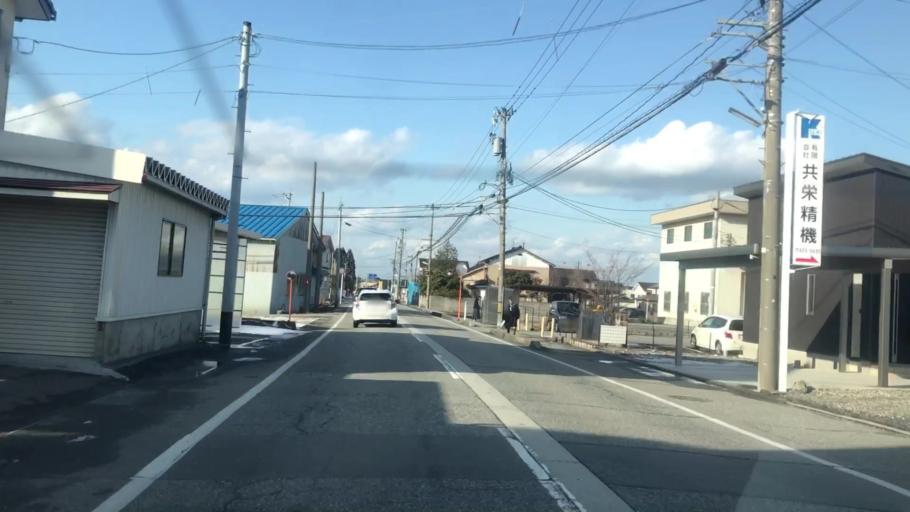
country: JP
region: Toyama
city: Toyama-shi
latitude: 36.6818
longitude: 137.2728
